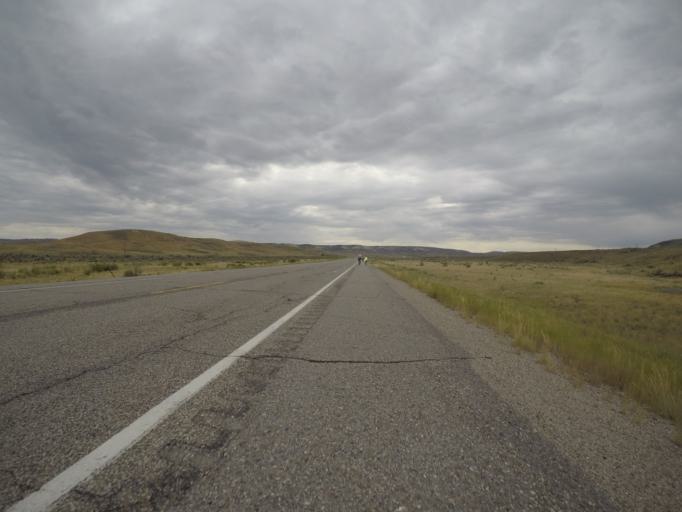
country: US
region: Wyoming
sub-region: Lincoln County
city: Kemmerer
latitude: 41.8125
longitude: -110.7003
